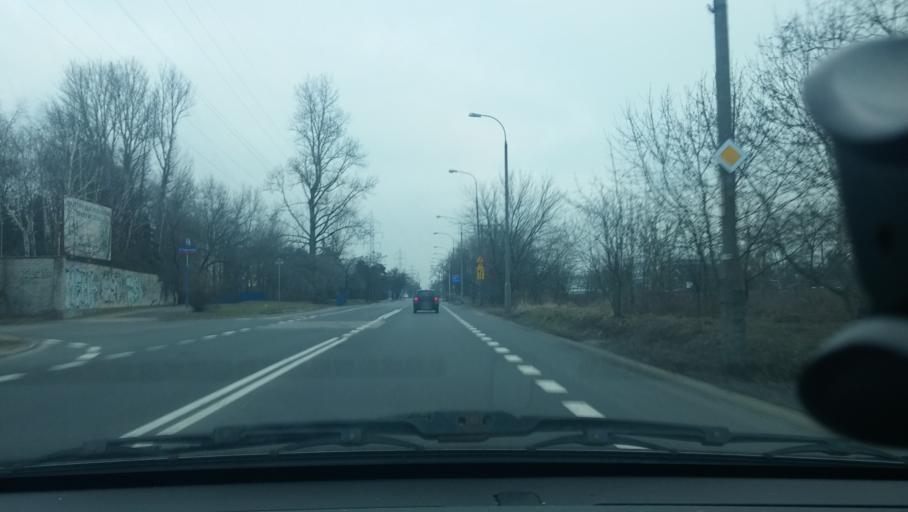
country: PL
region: Masovian Voivodeship
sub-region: Warszawa
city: Wawer
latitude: 52.2161
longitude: 21.1573
